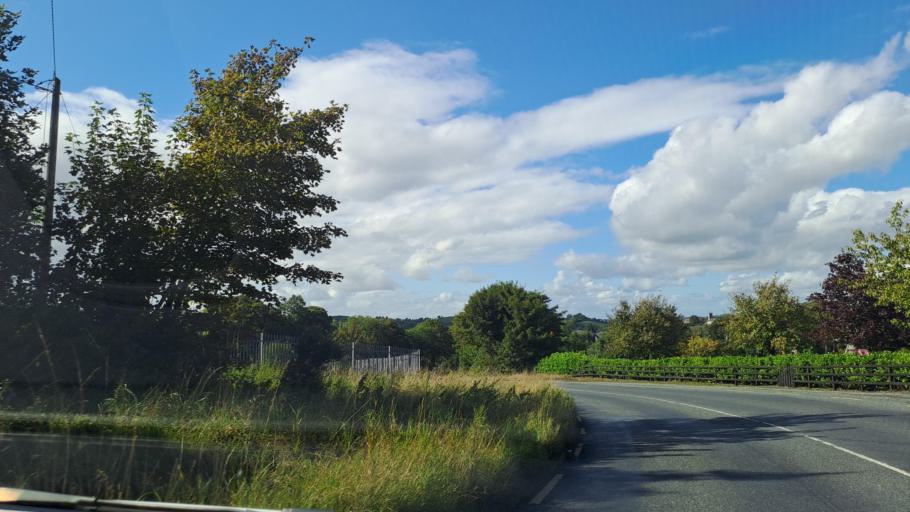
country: IE
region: Ulster
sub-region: An Cabhan
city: Bailieborough
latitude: 53.9891
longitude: -6.8842
